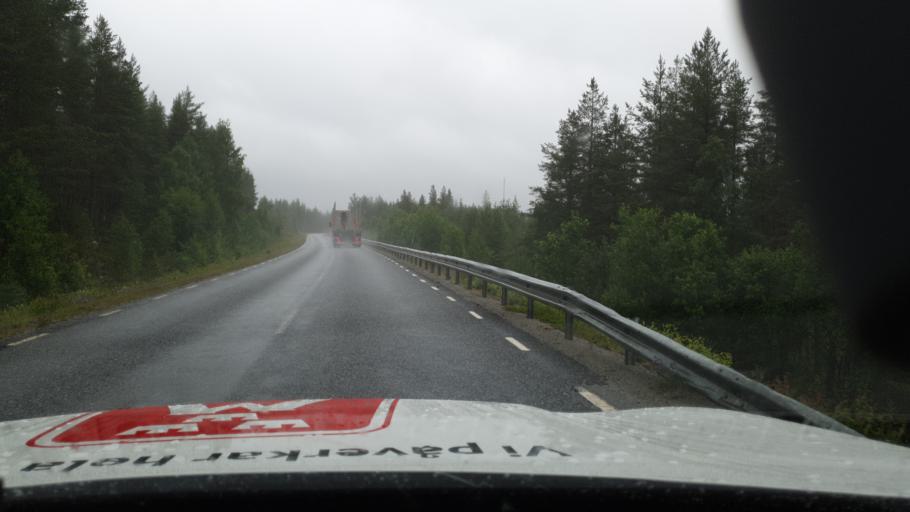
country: SE
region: Vaesterbotten
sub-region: Asele Kommun
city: Asele
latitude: 64.2912
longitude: 17.2599
